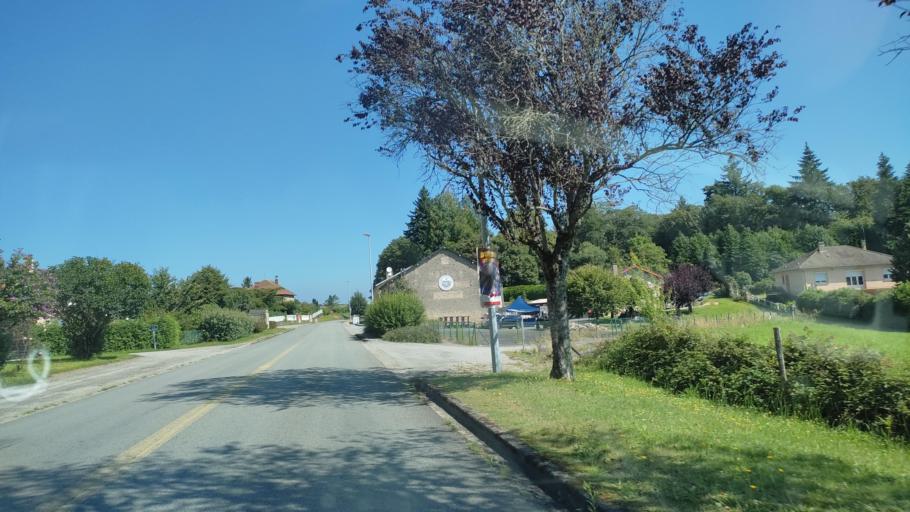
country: FR
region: Limousin
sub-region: Departement de la Haute-Vienne
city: Razes
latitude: 46.0277
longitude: 1.3446
